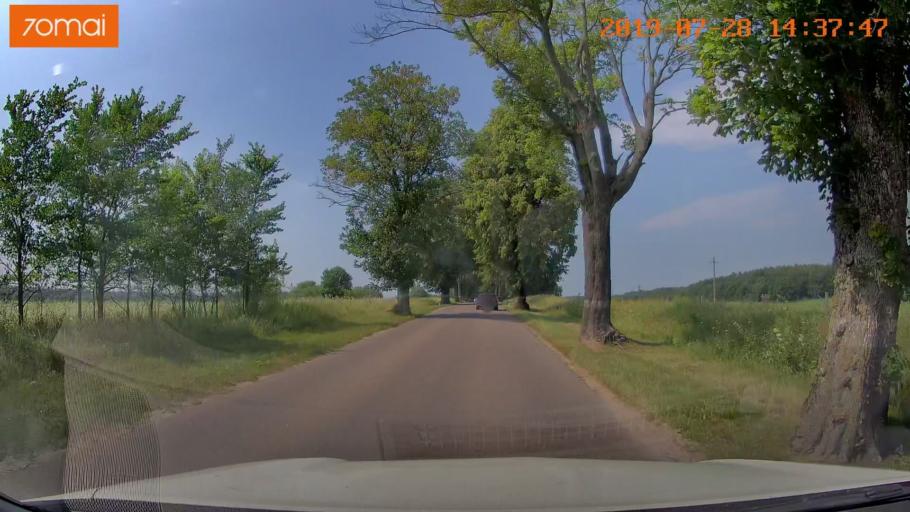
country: RU
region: Kaliningrad
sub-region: Gorod Kaliningrad
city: Yantarnyy
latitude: 54.8417
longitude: 19.9925
